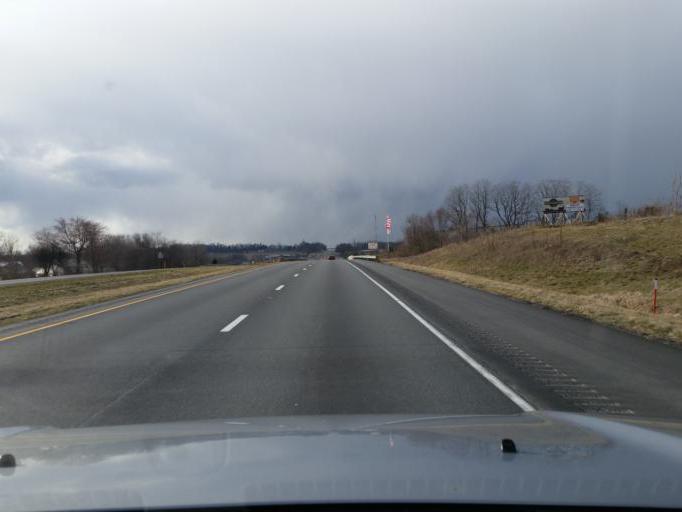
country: US
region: Pennsylvania
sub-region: Lancaster County
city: Rheems
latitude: 40.1384
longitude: -76.5486
